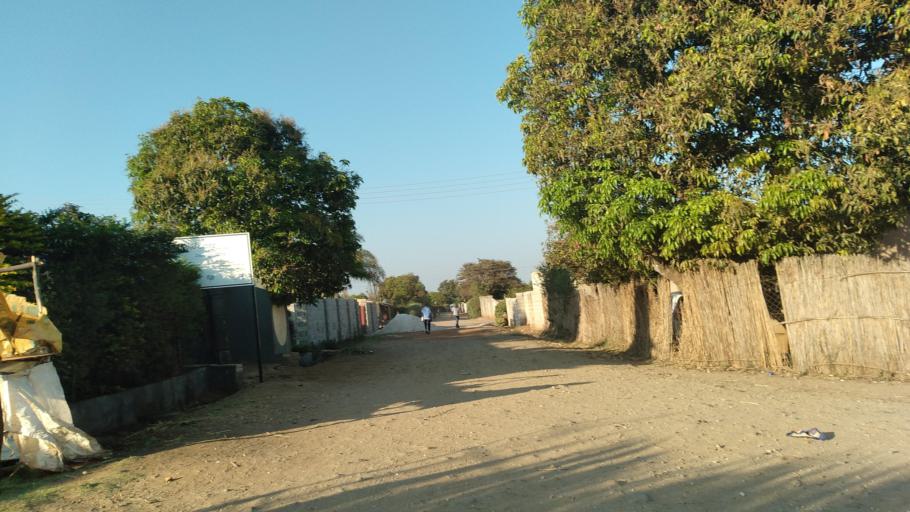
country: ZM
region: Lusaka
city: Lusaka
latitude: -15.5459
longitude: 28.2799
